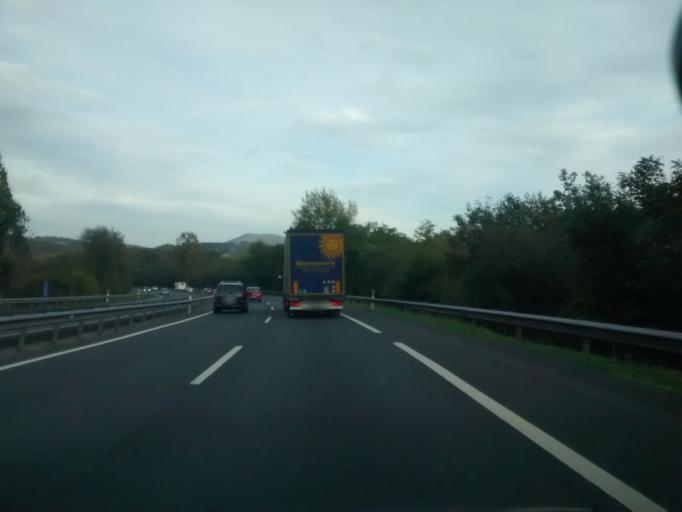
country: ES
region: Basque Country
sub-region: Provincia de Guipuzcoa
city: Cestona
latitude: 43.2593
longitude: -2.2868
